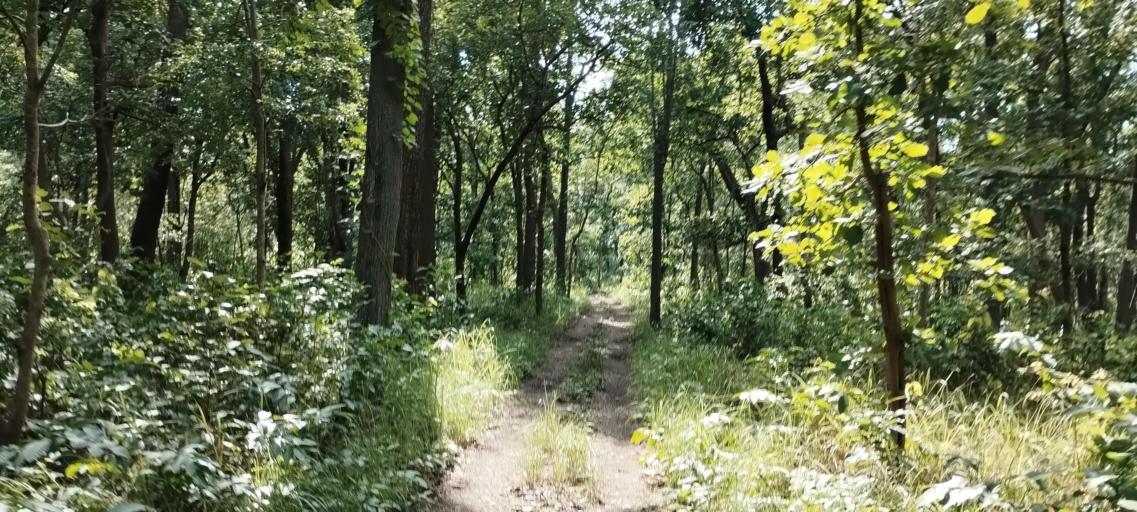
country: NP
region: Far Western
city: Tikapur
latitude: 28.5651
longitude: 81.2807
